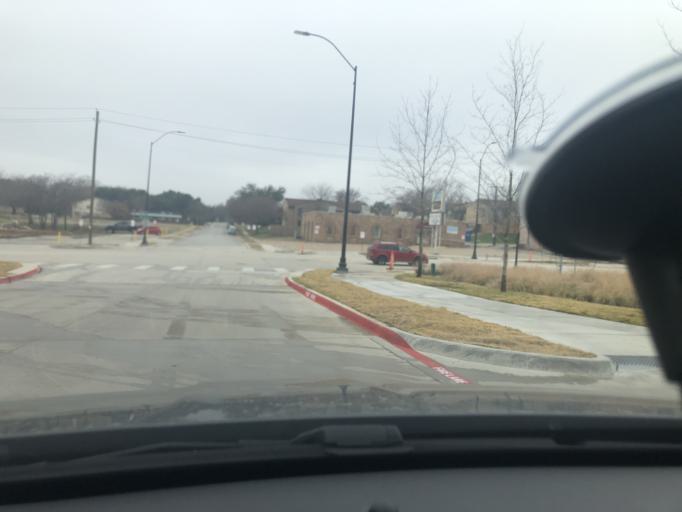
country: US
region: Texas
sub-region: Tarrant County
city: River Oaks
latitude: 32.7398
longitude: -97.3695
